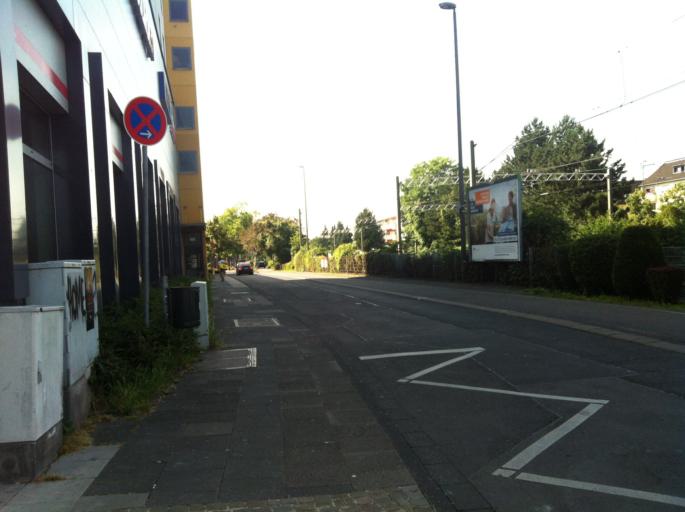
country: DE
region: North Rhine-Westphalia
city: Wesseling
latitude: 50.8230
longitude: 6.9787
